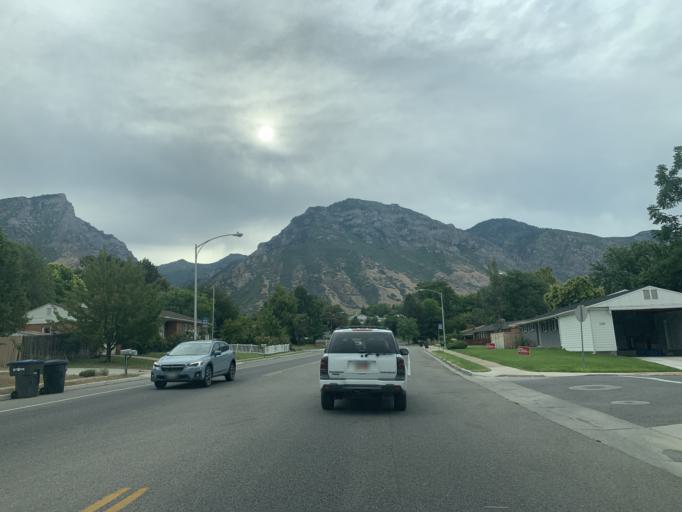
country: US
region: Utah
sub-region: Utah County
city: Provo
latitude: 40.2633
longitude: -111.6538
